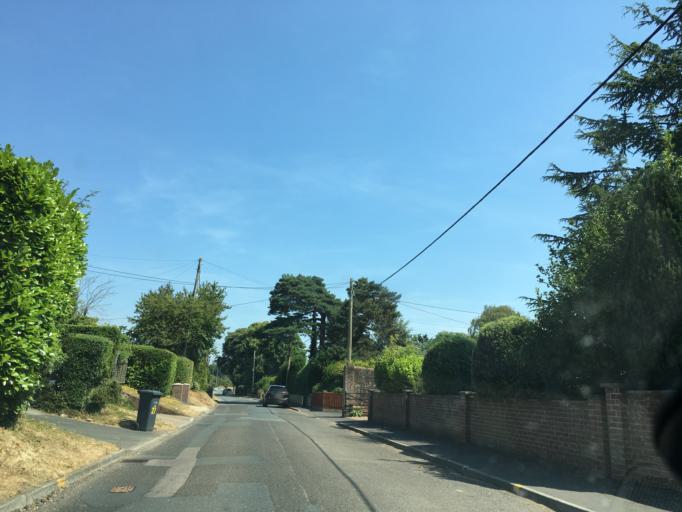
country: GB
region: England
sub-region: Isle of Wight
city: Newport
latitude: 50.7264
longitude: -1.2361
